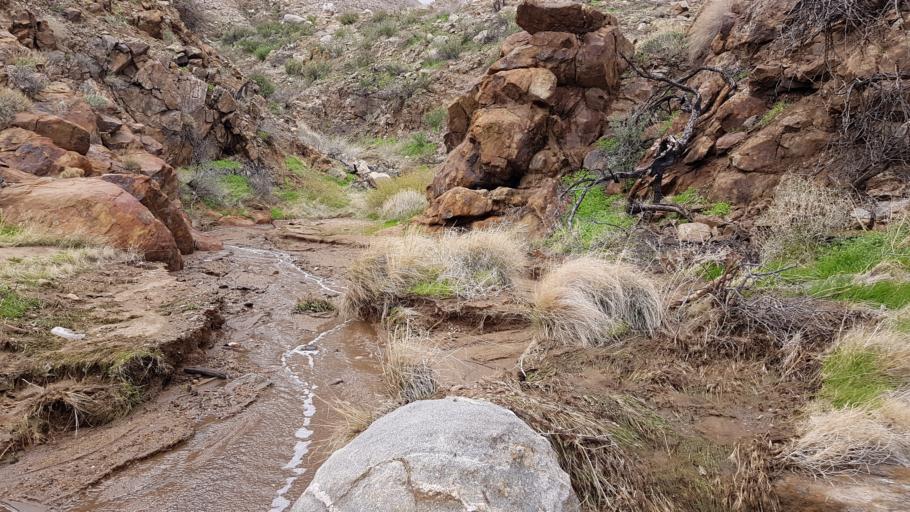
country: US
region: California
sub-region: San Diego County
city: Julian
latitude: 33.1348
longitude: -116.4664
